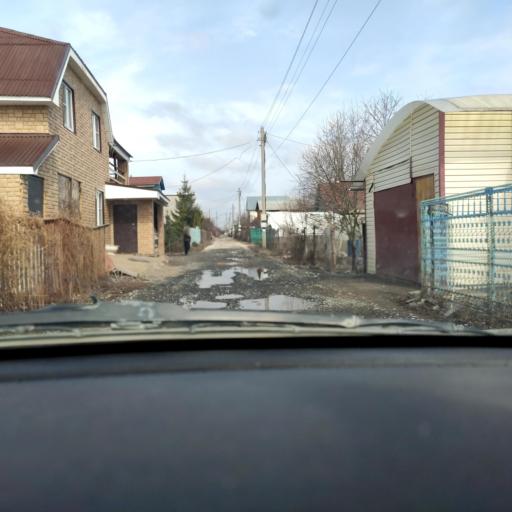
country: RU
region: Samara
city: Tol'yatti
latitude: 53.5838
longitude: 49.2898
